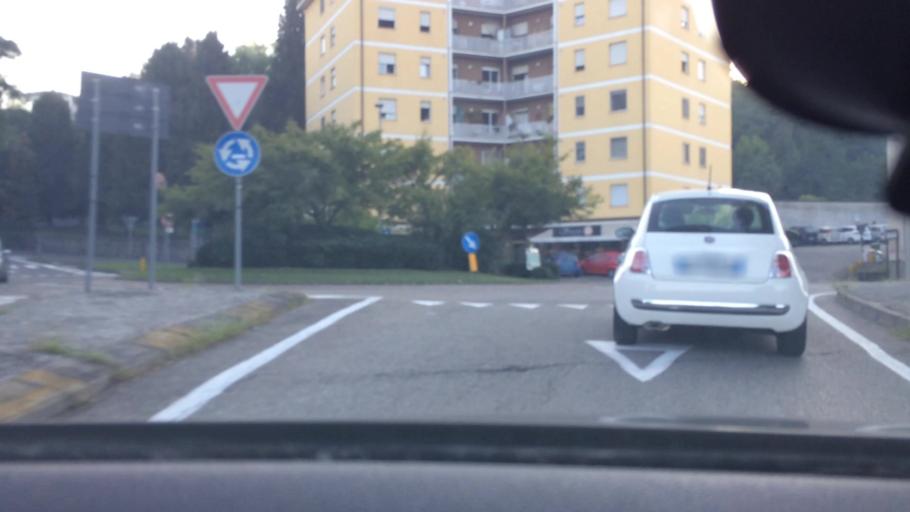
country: IT
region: Lombardy
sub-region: Provincia di Como
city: Cadorago-Caslino al Piano
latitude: 45.7290
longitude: 9.0406
